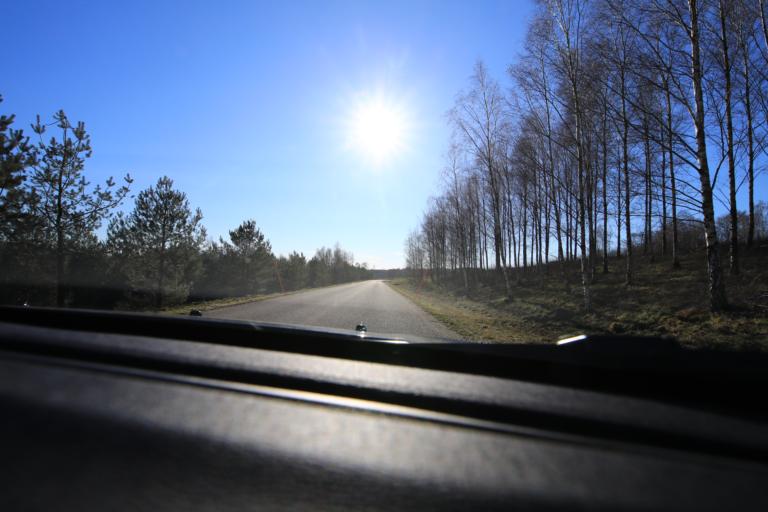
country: SE
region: Halland
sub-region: Varbergs Kommun
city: Tvaaker
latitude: 57.0683
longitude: 12.4683
